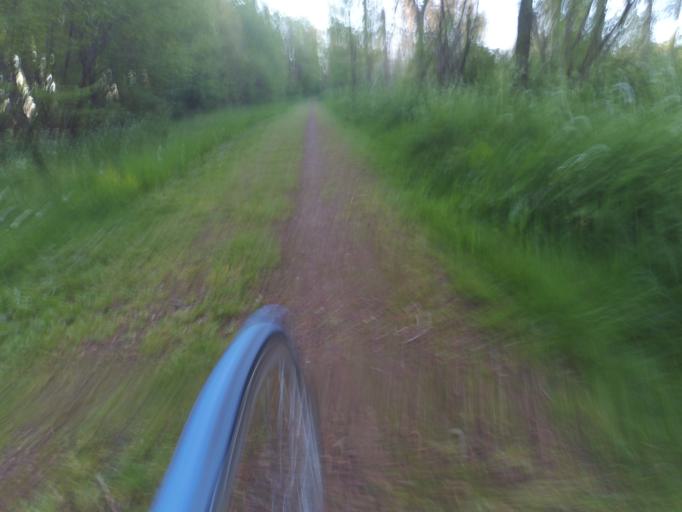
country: NL
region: Flevoland
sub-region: Gemeente Lelystad
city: Lelystad
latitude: 52.4309
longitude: 5.4983
